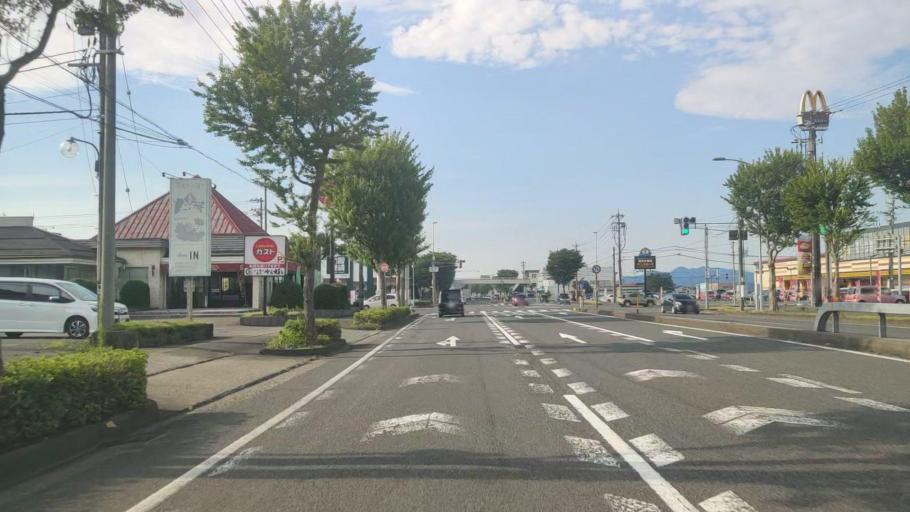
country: JP
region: Fukui
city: Takefu
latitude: 35.9074
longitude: 136.1921
